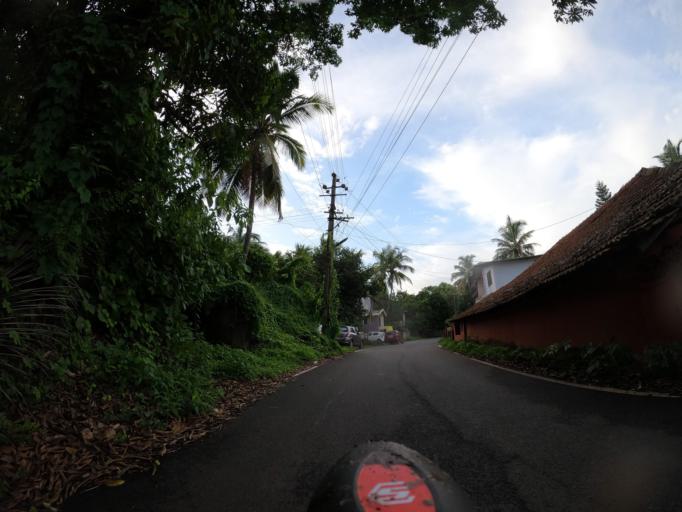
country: IN
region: Goa
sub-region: North Goa
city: Panaji
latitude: 15.5160
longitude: 73.8453
